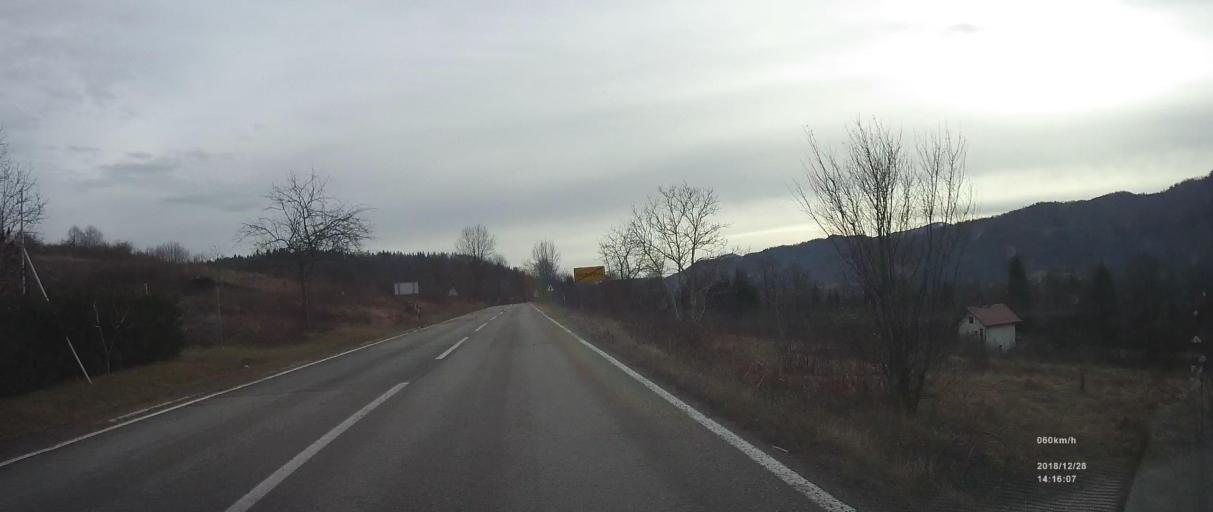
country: HR
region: Primorsko-Goranska
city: Vrbovsko
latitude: 45.4212
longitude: 15.0336
